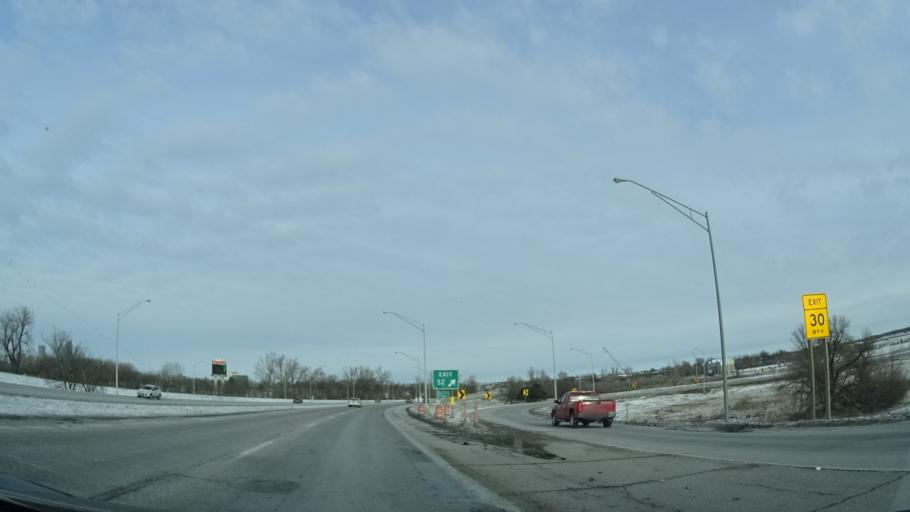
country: US
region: Nebraska
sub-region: Douglas County
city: Omaha
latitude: 41.2432
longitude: -95.9055
